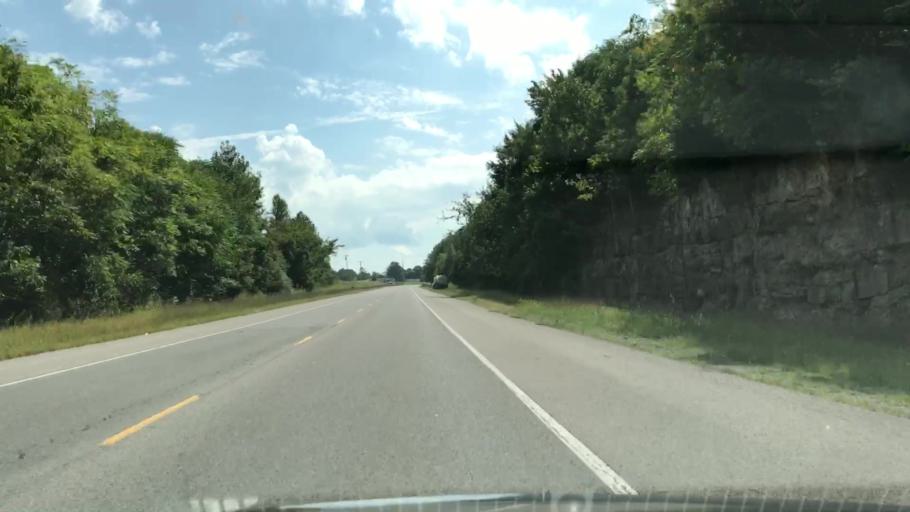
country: US
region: Tennessee
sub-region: Sumner County
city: Westmoreland
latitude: 36.5448
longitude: -86.2154
